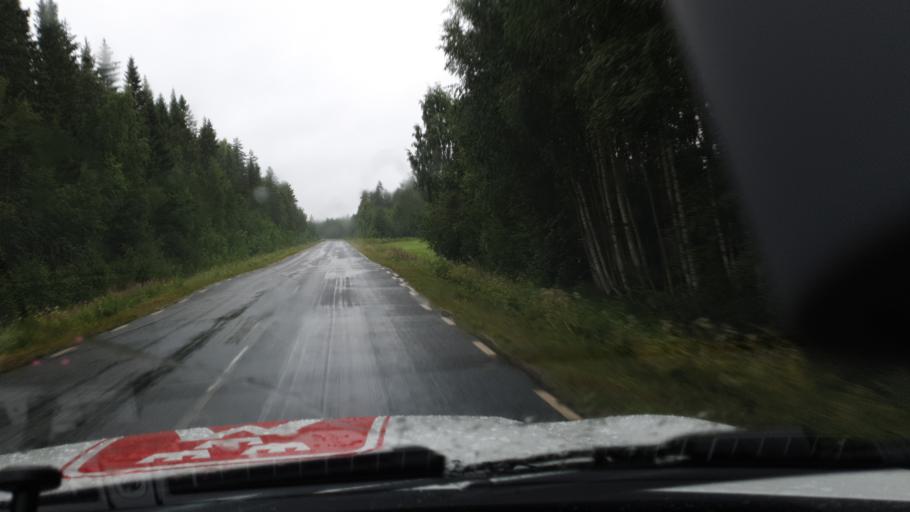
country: SE
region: Vaesterbotten
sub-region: Skelleftea Kommun
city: Soedra Bergsbyn
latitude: 64.5943
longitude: 21.0624
